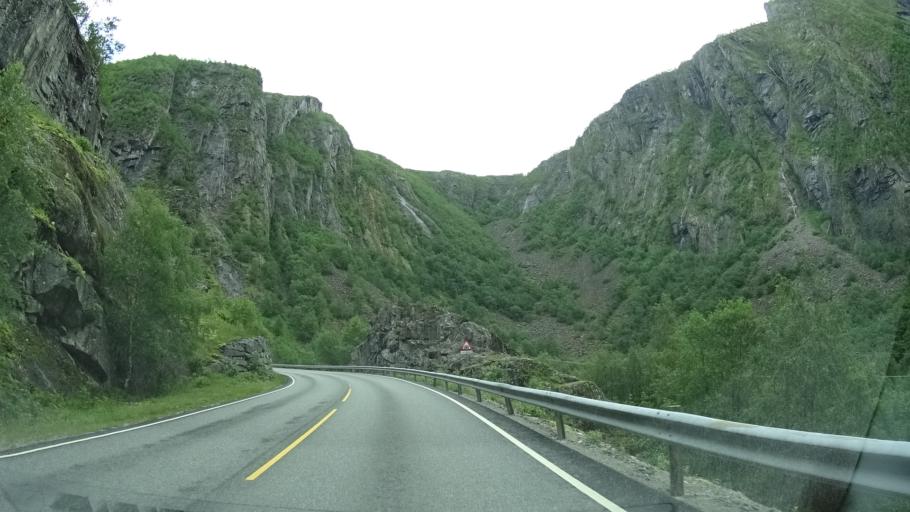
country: NO
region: Hordaland
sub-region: Eidfjord
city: Eidfjord
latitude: 60.4179
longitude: 7.2050
